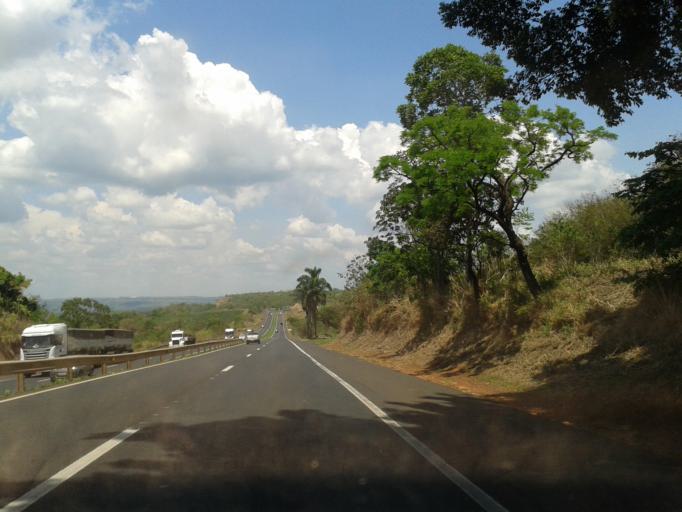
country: BR
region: Minas Gerais
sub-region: Araguari
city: Araguari
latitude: -18.7160
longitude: -48.1990
